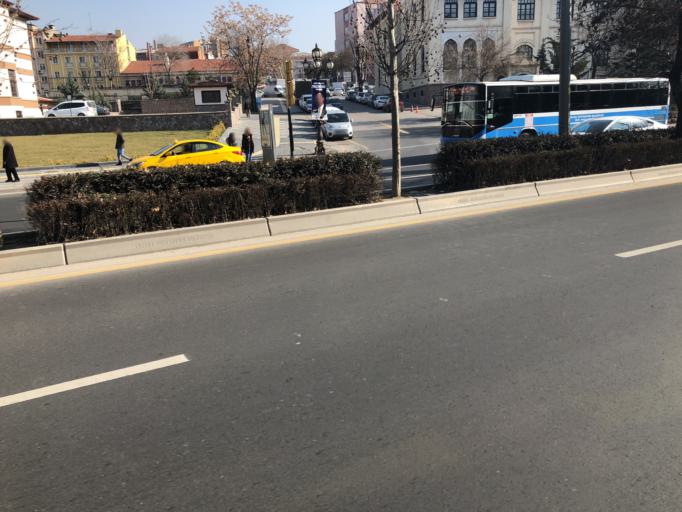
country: TR
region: Ankara
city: Ankara
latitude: 39.9356
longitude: 32.8542
